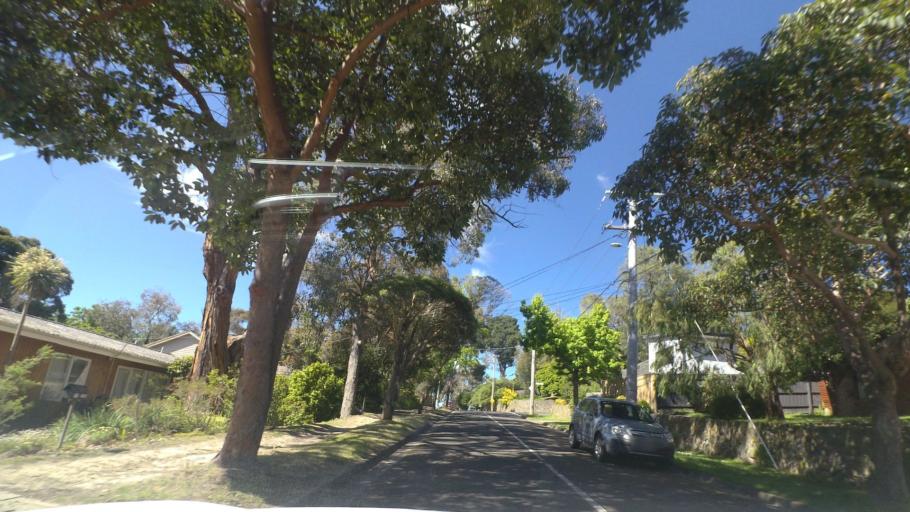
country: AU
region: Victoria
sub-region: Maroondah
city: Ringwood East
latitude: -37.8199
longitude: 145.2580
